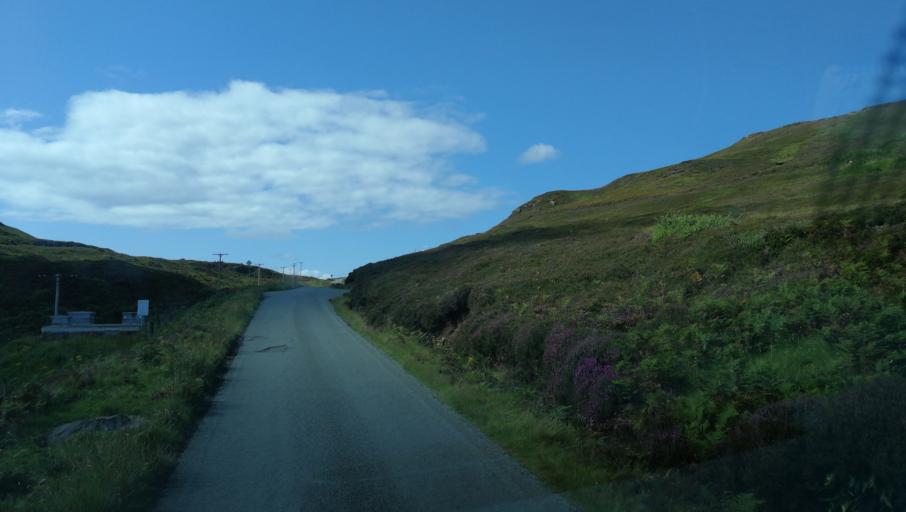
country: GB
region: Scotland
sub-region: Highland
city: Isle of Skye
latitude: 57.4499
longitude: -6.6746
